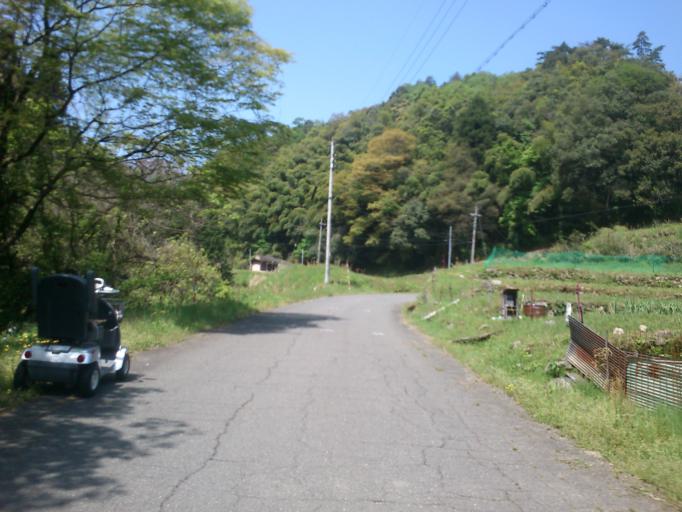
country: JP
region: Kyoto
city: Miyazu
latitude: 35.6111
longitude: 135.2012
